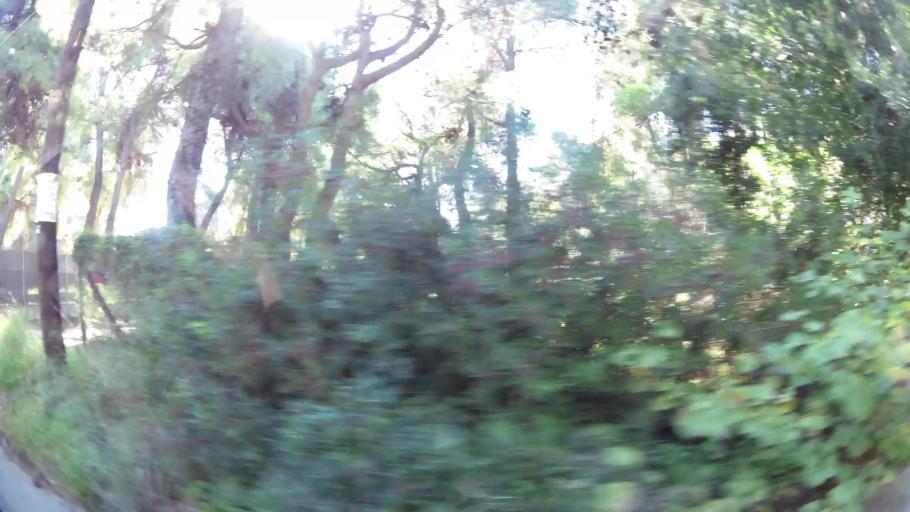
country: GR
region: Attica
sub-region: Nomarchia Athinas
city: Ekali
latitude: 38.1069
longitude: 23.8281
